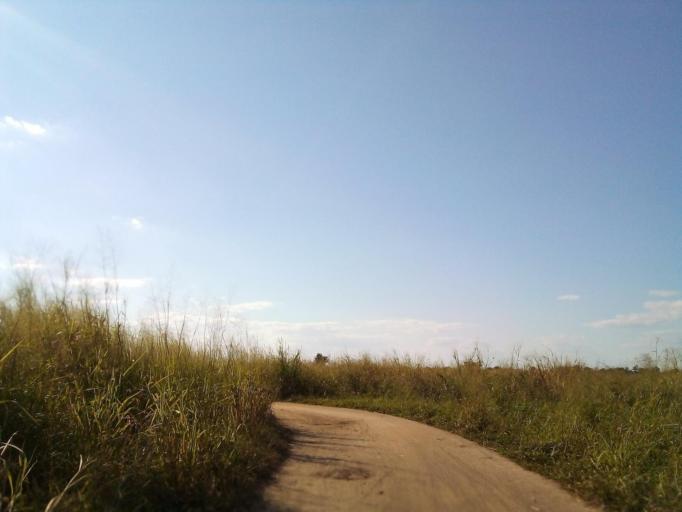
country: MZ
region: Zambezia
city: Quelimane
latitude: -17.5459
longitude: 36.6949
